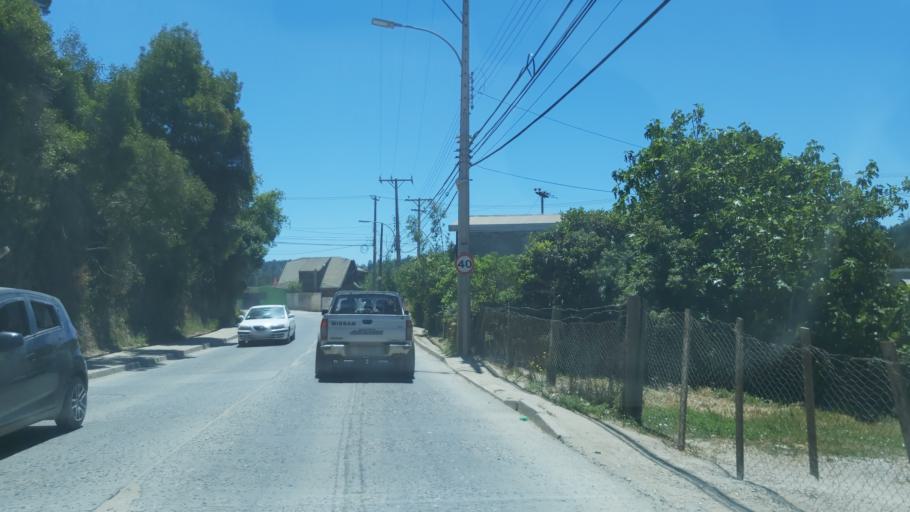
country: CL
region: Maule
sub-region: Provincia de Talca
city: Constitucion
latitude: -35.3414
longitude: -72.3965
